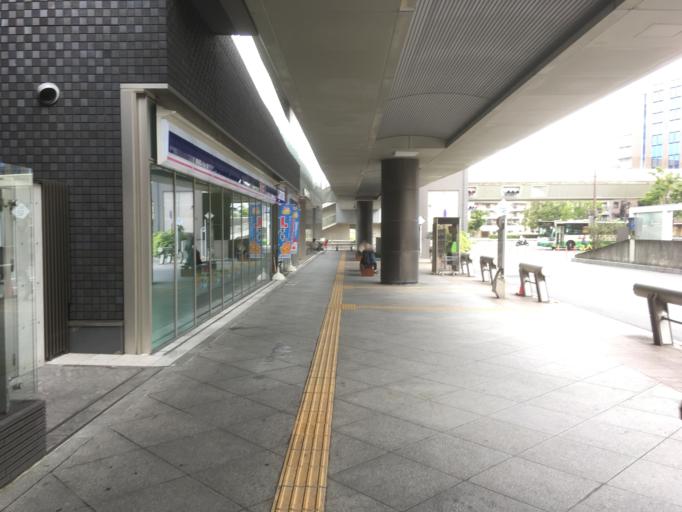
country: JP
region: Nara
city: Nara-shi
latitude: 34.6806
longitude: 135.8183
